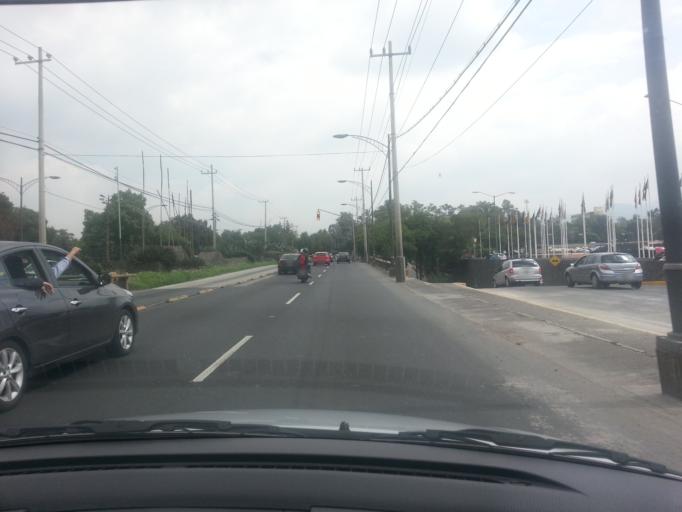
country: MX
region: Mexico City
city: Magdalena Contreras
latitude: 19.3330
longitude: -99.1899
